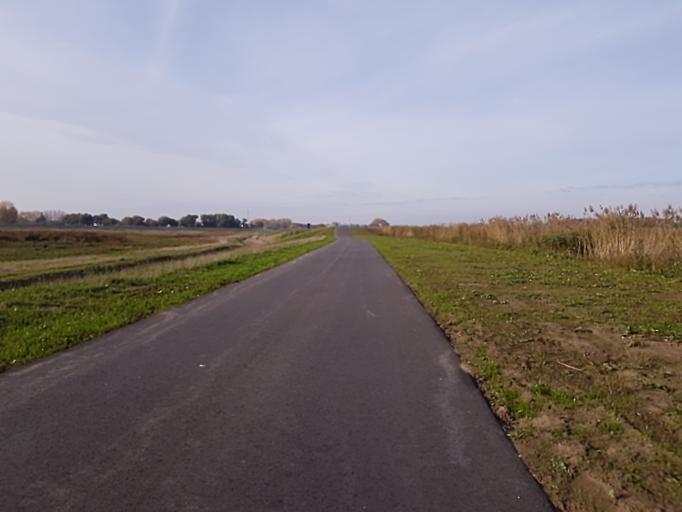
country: BE
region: Flanders
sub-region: Provincie Antwerpen
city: Rumst
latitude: 51.0597
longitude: 4.4401
